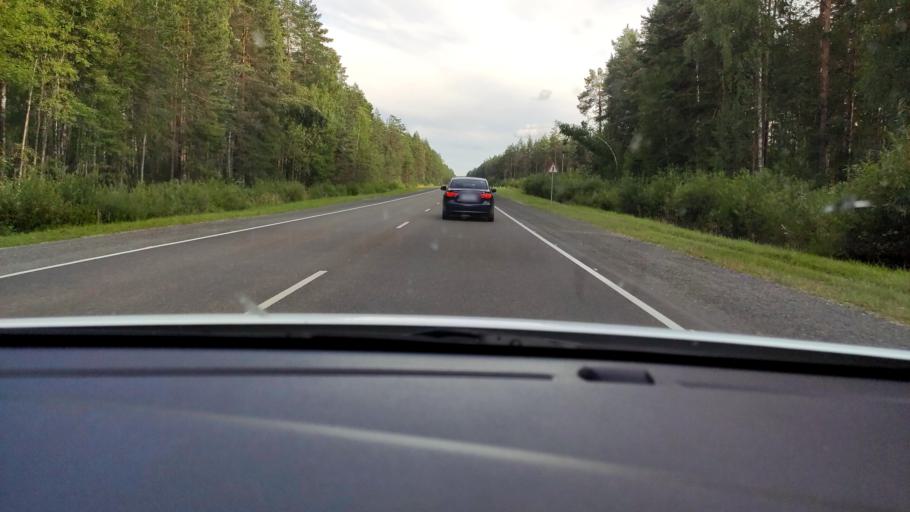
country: RU
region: Mariy-El
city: Suslonger
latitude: 56.3544
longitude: 48.2214
